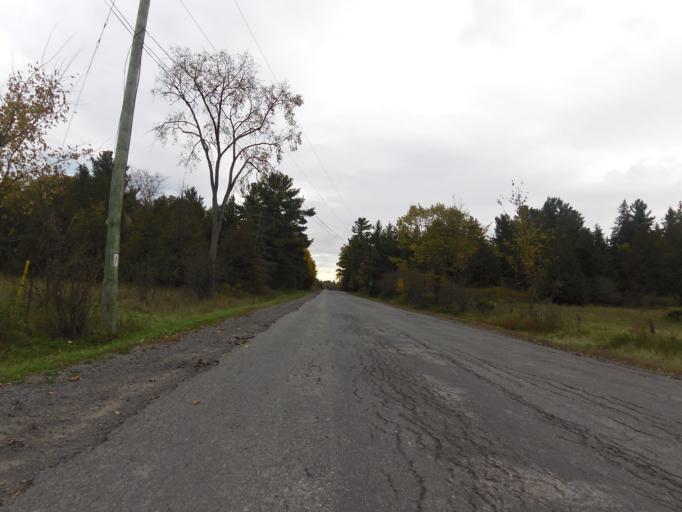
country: CA
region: Ontario
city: Arnprior
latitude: 45.4592
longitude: -76.1423
